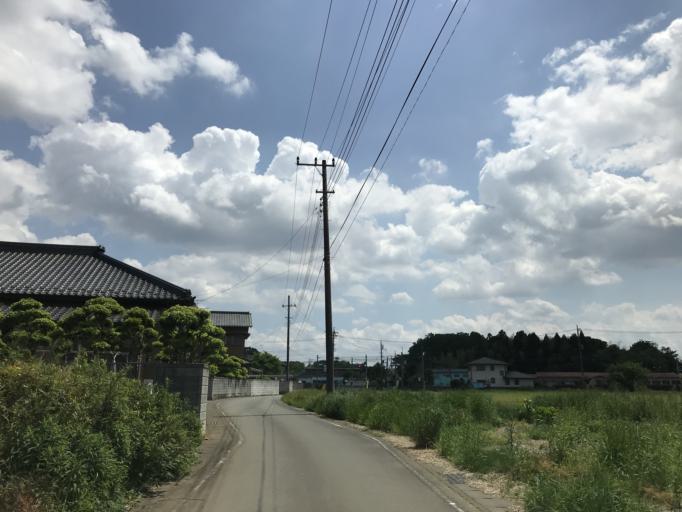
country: JP
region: Ibaraki
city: Mitsukaido
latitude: 36.0693
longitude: 140.0435
